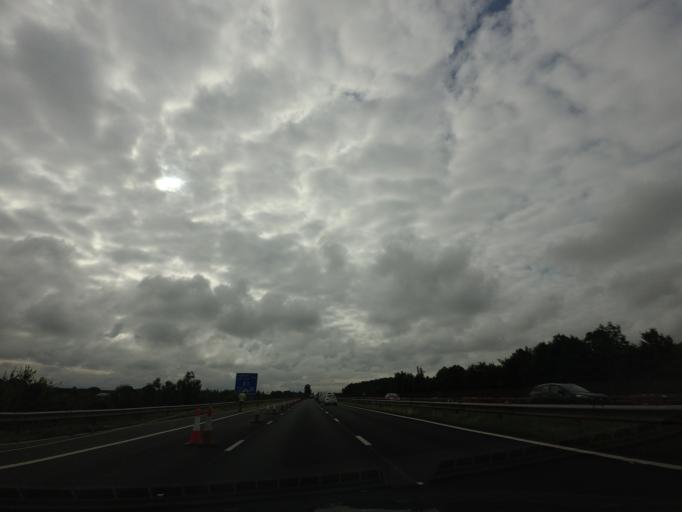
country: GB
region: Scotland
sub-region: Dumfries and Galloway
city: Gretna
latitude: 54.9622
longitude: -2.9932
